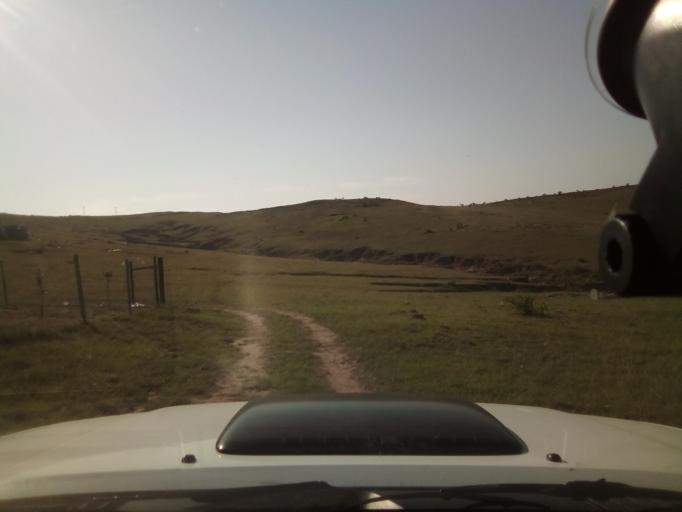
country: ZA
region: Eastern Cape
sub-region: Buffalo City Metropolitan Municipality
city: East London
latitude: -32.8409
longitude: 27.9963
